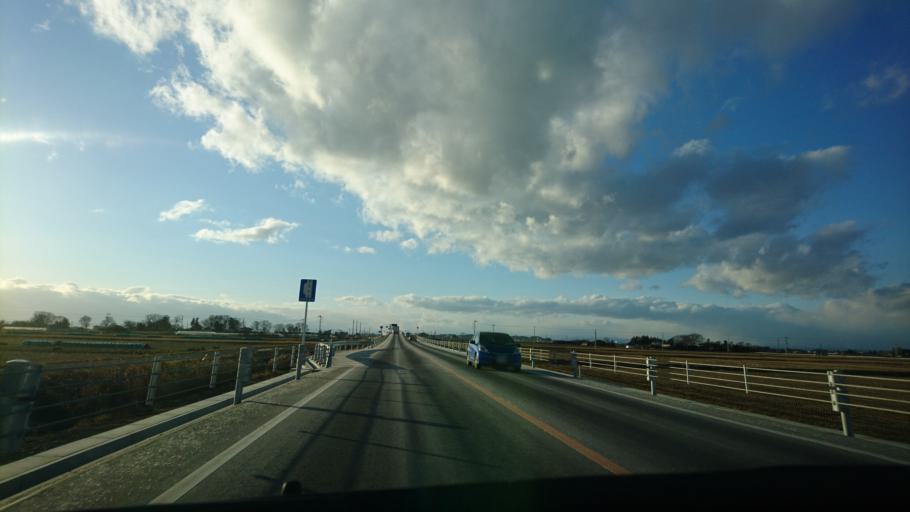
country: JP
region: Miyagi
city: Wakuya
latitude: 38.6856
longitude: 141.2417
